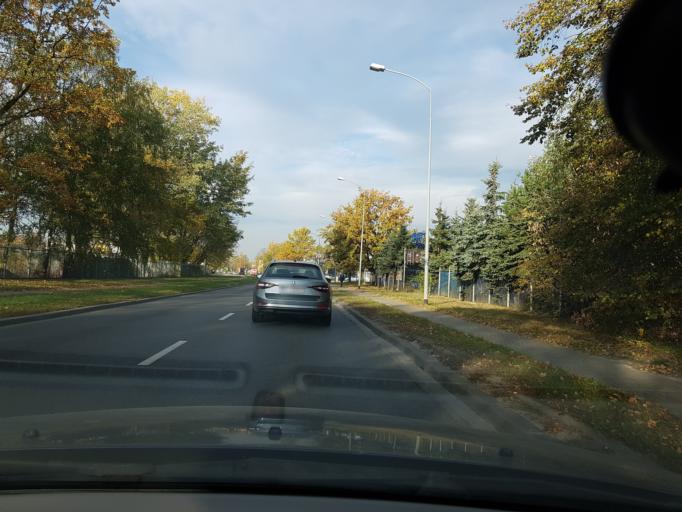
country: PL
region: Masovian Voivodeship
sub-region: Warszawa
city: Bielany
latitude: 52.2835
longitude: 20.9125
